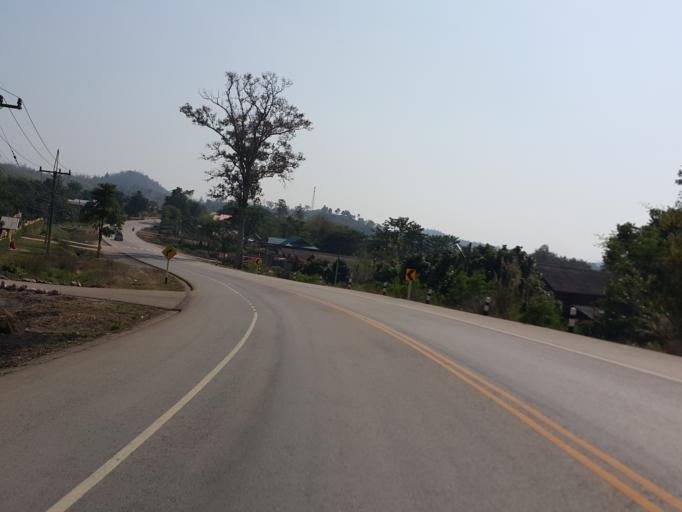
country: TH
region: Lampang
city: Mueang Pan
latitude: 18.9024
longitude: 99.6054
